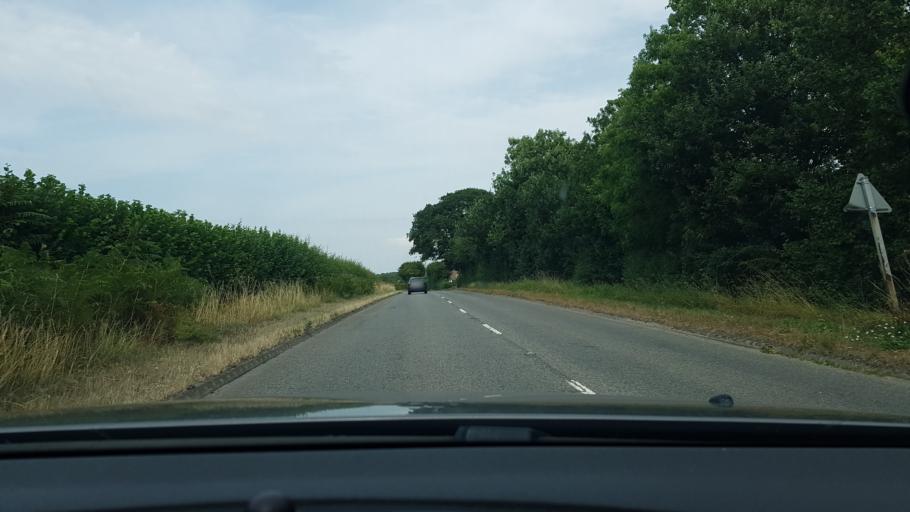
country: GB
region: England
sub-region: Wiltshire
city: Shalbourne
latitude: 51.3837
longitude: -1.5322
